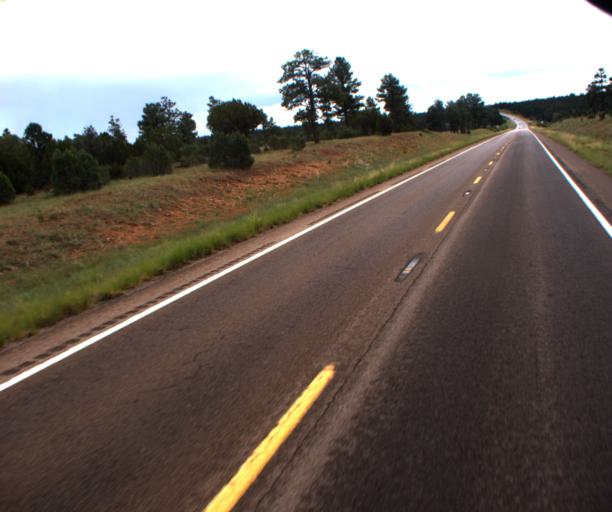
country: US
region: Arizona
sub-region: Navajo County
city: Heber-Overgaard
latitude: 34.3871
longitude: -110.5000
